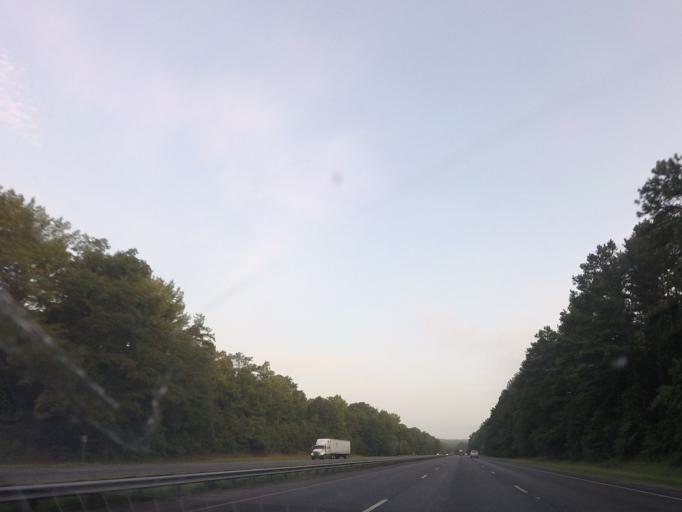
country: US
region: Georgia
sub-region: Monroe County
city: Forsyth
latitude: 33.0755
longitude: -83.9814
